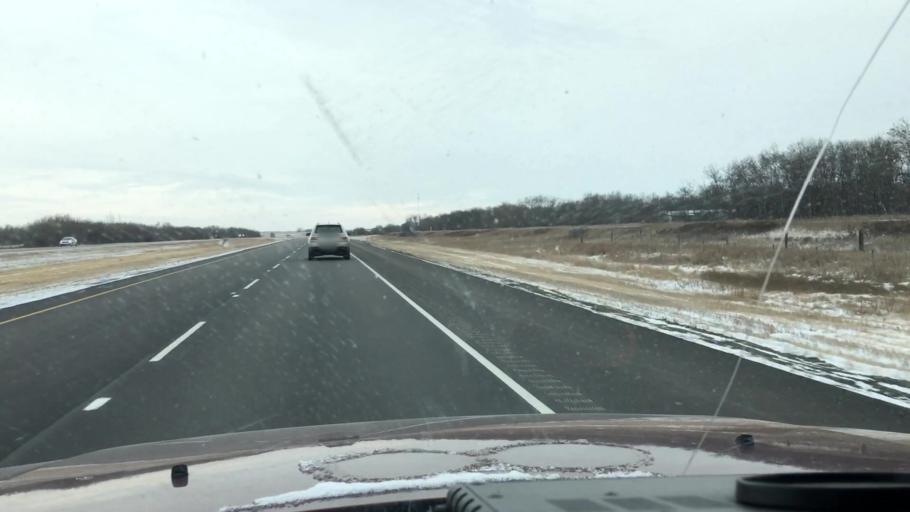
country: CA
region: Saskatchewan
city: Saskatoon
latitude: 51.8779
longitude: -106.5111
